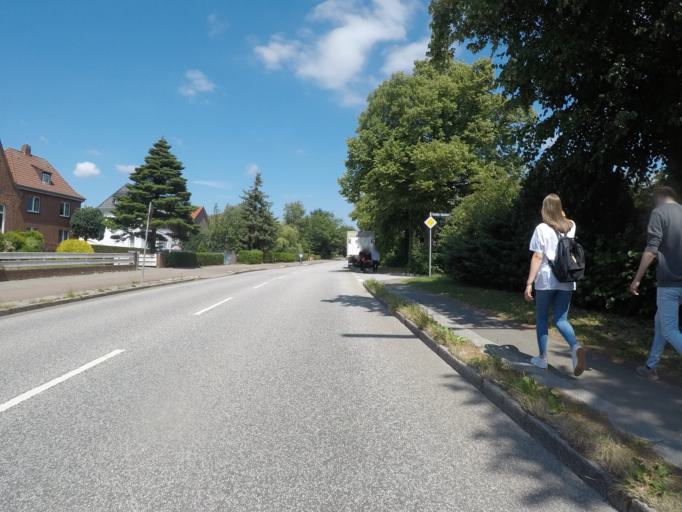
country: DE
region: Hamburg
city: Kleiner Grasbrook
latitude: 53.4931
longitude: 10.0194
